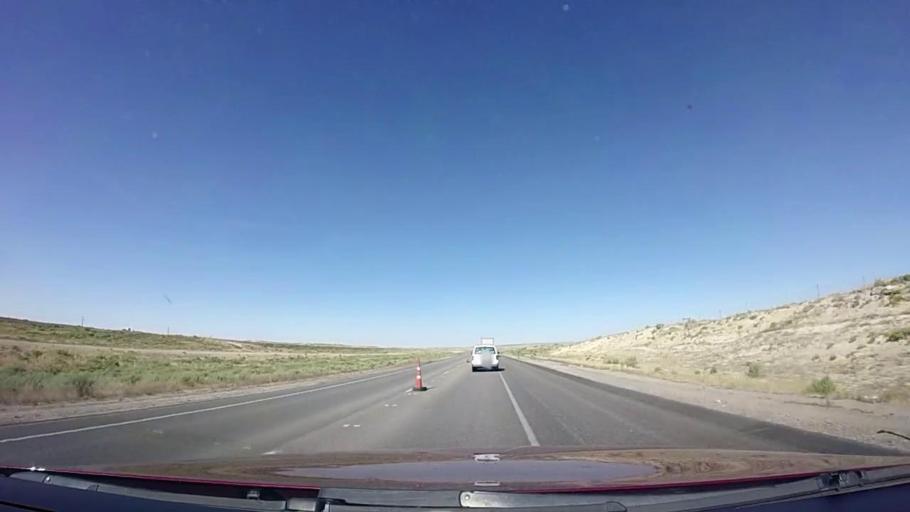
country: US
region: Wyoming
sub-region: Carbon County
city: Rawlins
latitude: 41.7067
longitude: -107.8710
